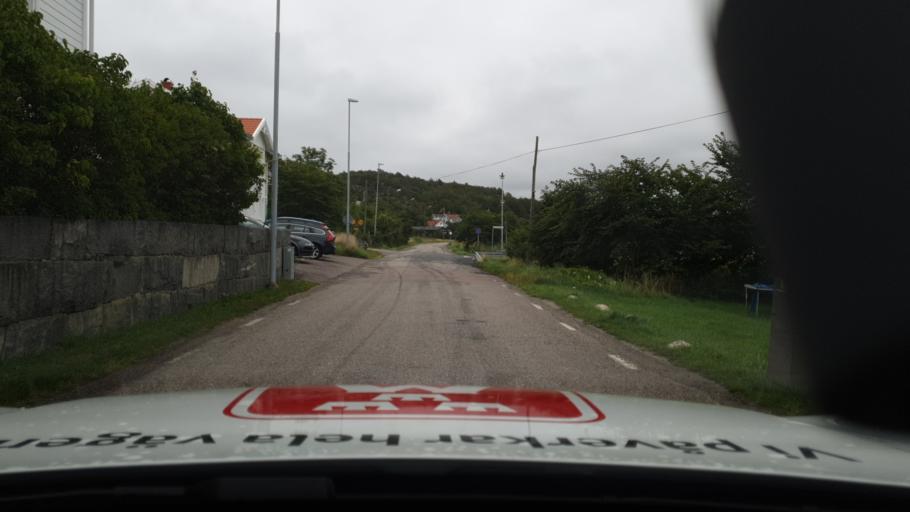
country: SE
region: Vaestra Goetaland
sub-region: Kungalvs Kommun
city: Kode
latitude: 57.8994
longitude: 11.7183
